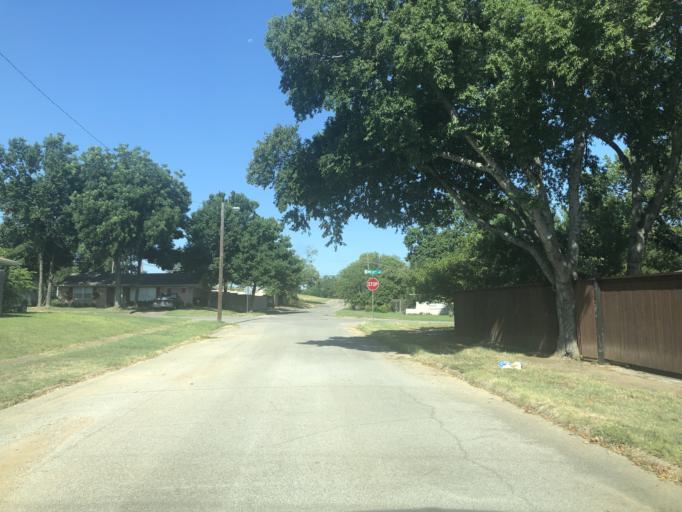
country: US
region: Texas
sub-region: Dallas County
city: Grand Prairie
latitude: 32.7521
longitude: -97.0219
